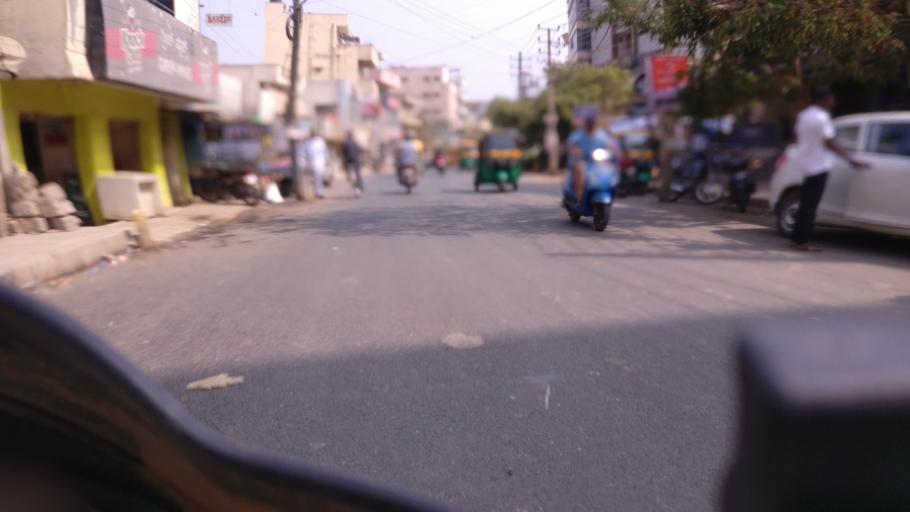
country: IN
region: Karnataka
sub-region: Bangalore Urban
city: Bangalore
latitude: 12.9073
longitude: 77.6758
